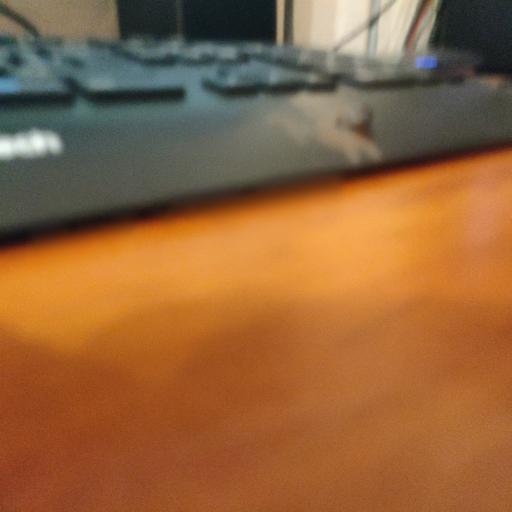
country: SE
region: Vaestmanland
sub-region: Vasteras
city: Tillberga
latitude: 59.6942
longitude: 16.6769
